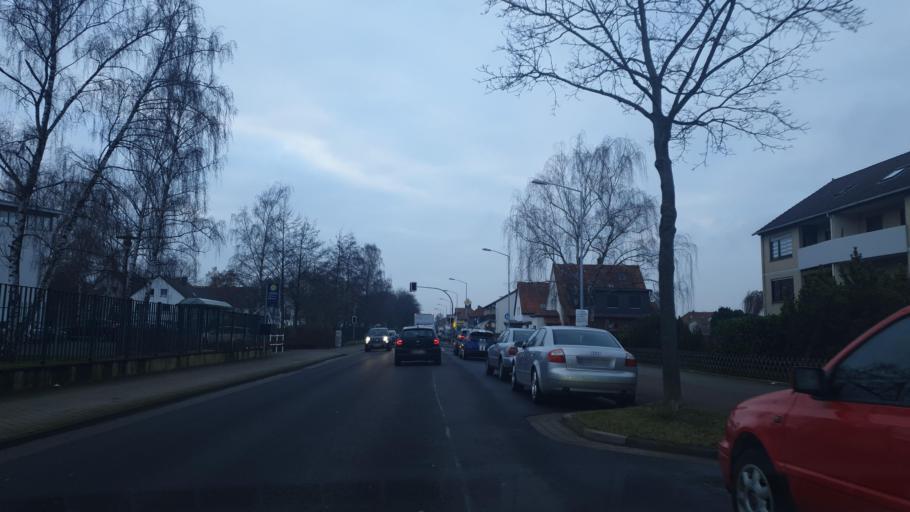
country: DE
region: Lower Saxony
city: Buckeburg
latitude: 52.2618
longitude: 9.0395
